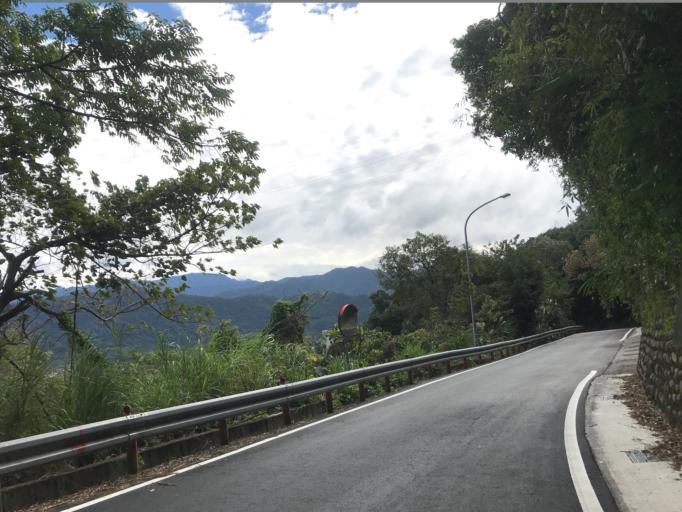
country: TW
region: Taiwan
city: Daxi
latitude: 24.8358
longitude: 121.2448
